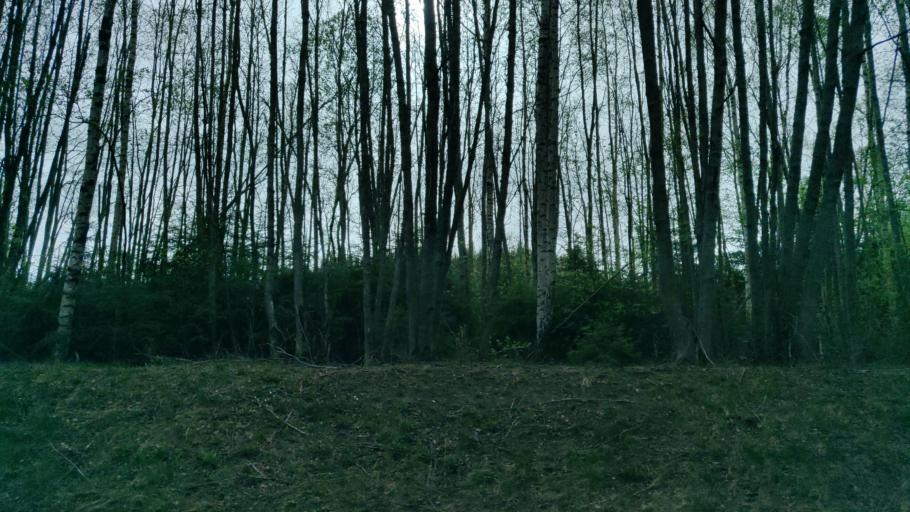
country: SE
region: Vaermland
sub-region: Forshaga Kommun
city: Deje
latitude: 59.6486
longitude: 13.4422
